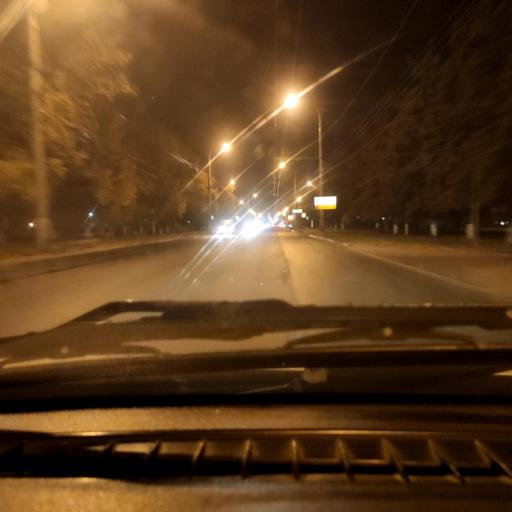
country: RU
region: Samara
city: Tol'yatti
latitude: 53.5374
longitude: 49.4416
